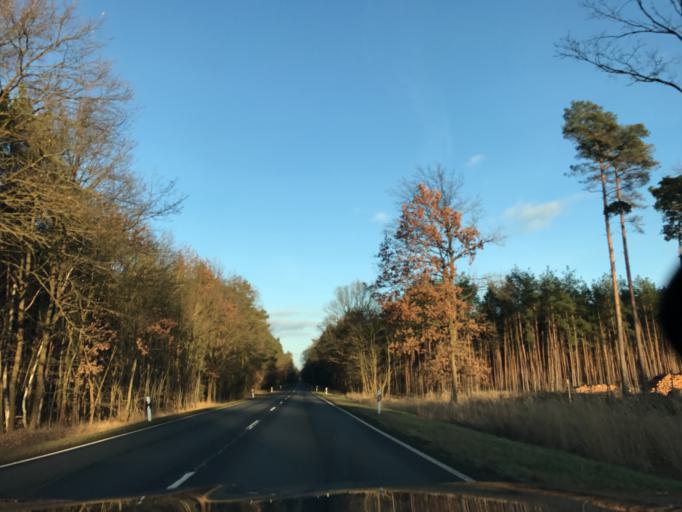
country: DE
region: Saxony-Anhalt
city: Genthin
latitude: 52.3217
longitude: 12.0242
